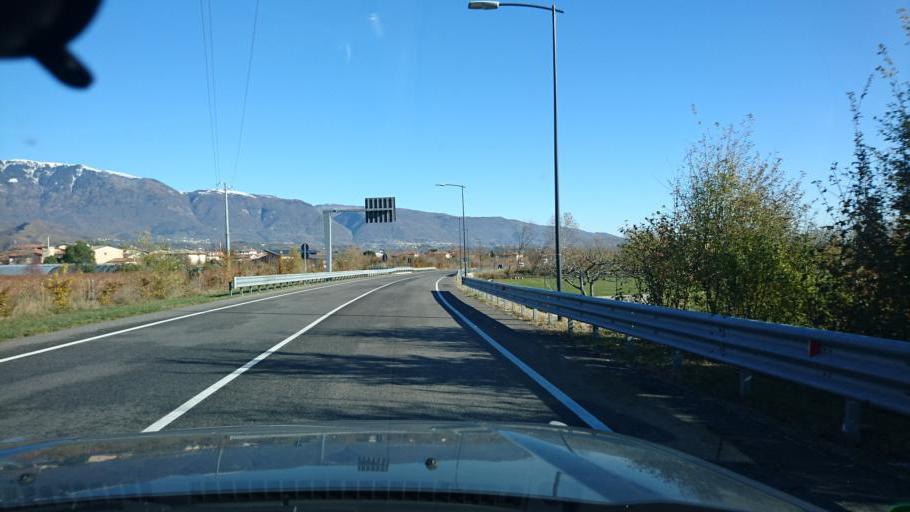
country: IT
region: Veneto
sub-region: Provincia di Treviso
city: Carpesica
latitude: 45.9652
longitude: 12.2901
